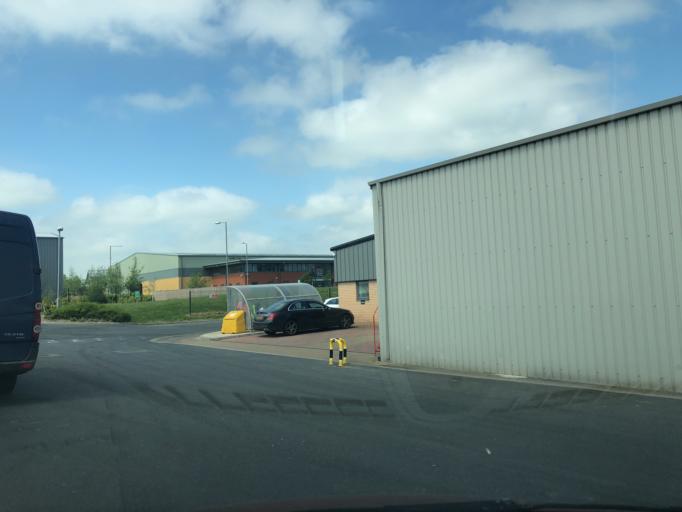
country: GB
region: England
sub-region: North Yorkshire
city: Bedale
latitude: 54.3077
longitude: -1.5664
